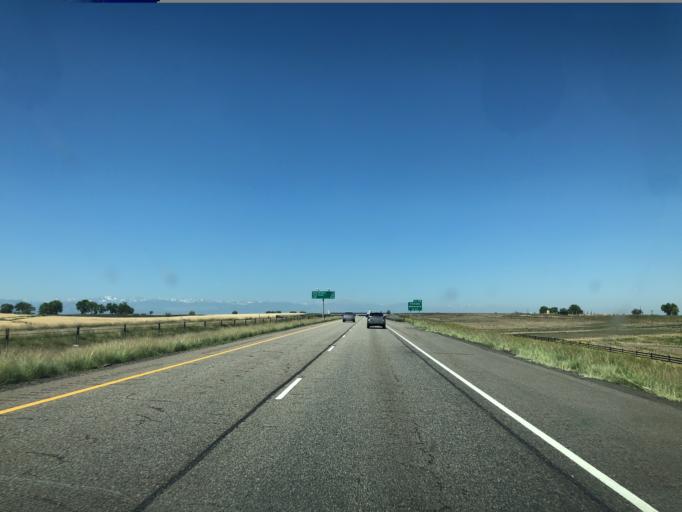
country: US
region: Colorado
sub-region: Adams County
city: Todd Creek
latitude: 39.9663
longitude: -104.9194
